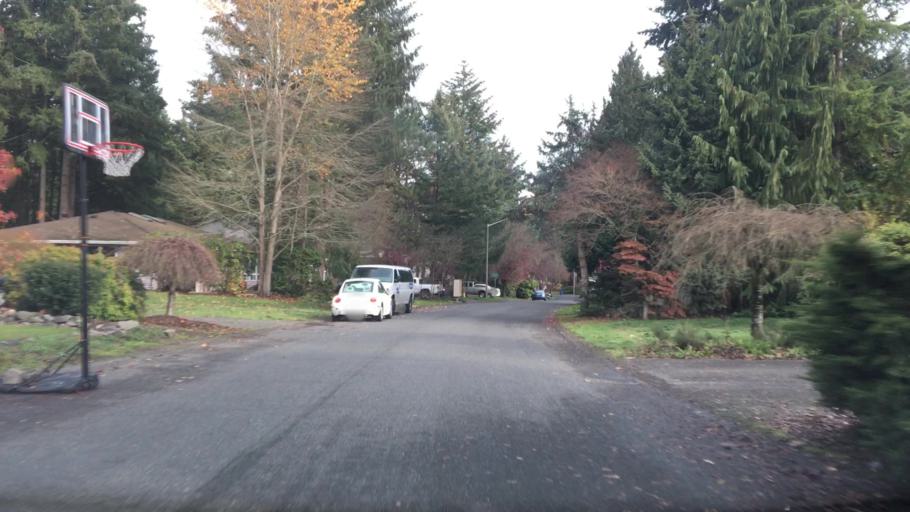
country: US
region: Washington
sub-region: Pierce County
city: South Hill
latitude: 47.1087
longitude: -122.3033
